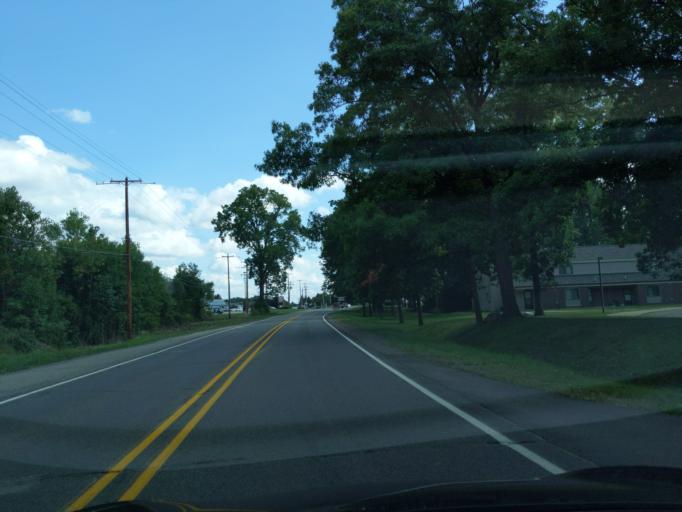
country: US
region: Michigan
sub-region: Jackson County
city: Jackson
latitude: 42.2787
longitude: -84.4543
